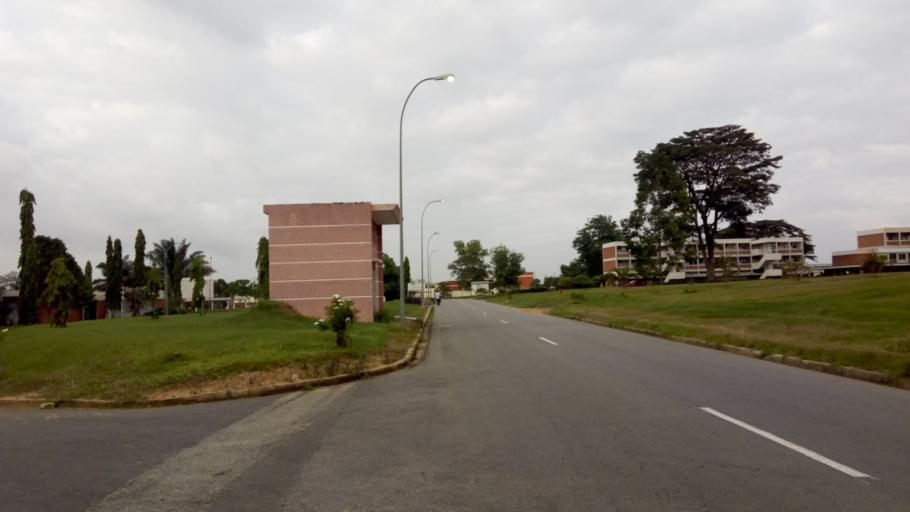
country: CI
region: Lagunes
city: Abidjan
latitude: 5.3448
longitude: -3.9852
